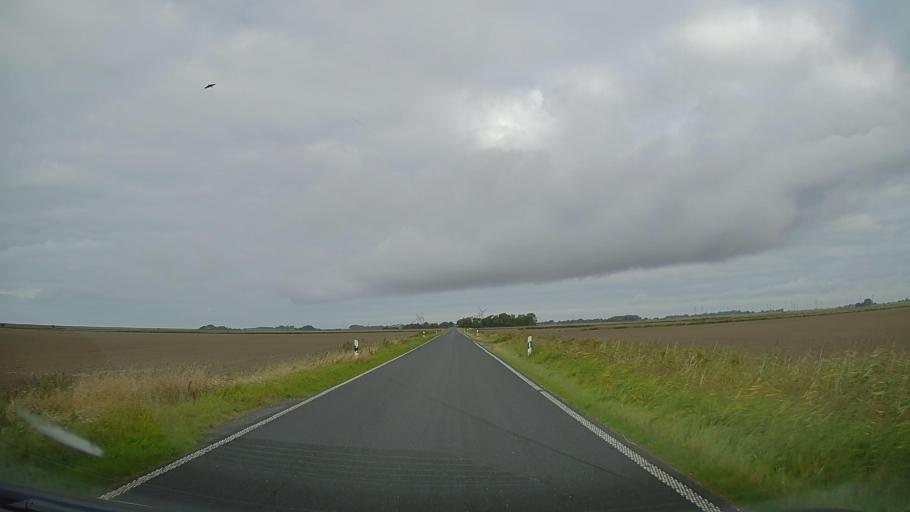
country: DE
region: Schleswig-Holstein
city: Galmsbull
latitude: 54.7474
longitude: 8.7337
